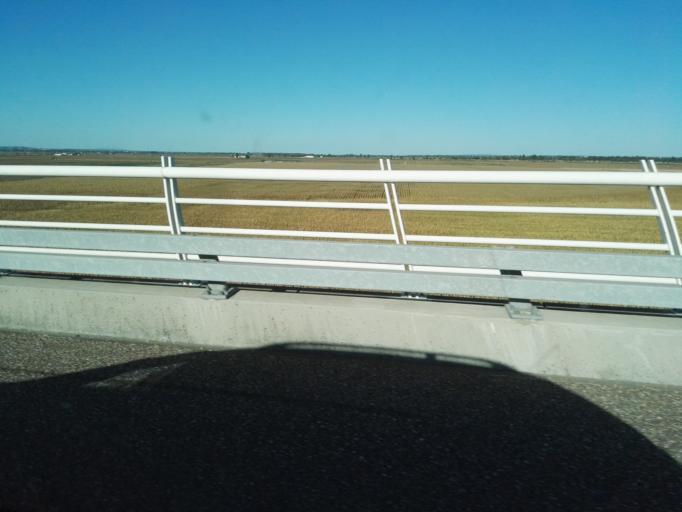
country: PT
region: Santarem
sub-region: Benavente
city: Samora Correia
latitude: 38.9780
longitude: -8.8821
